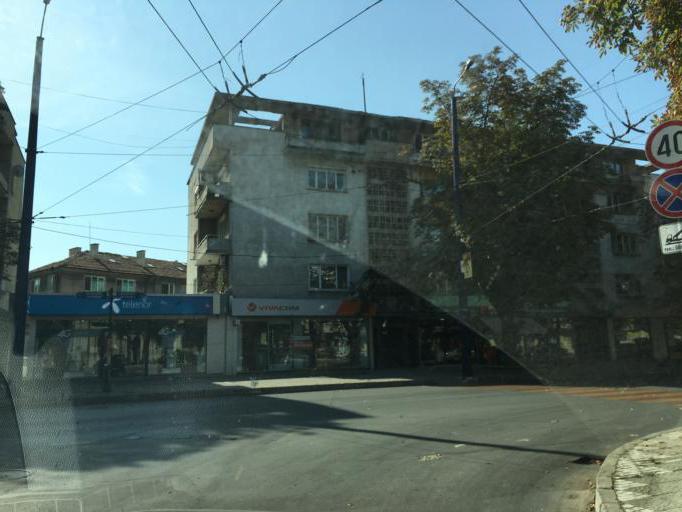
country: BG
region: Pazardzhik
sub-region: Obshtina Pazardzhik
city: Pazardzhik
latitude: 42.1888
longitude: 24.3316
